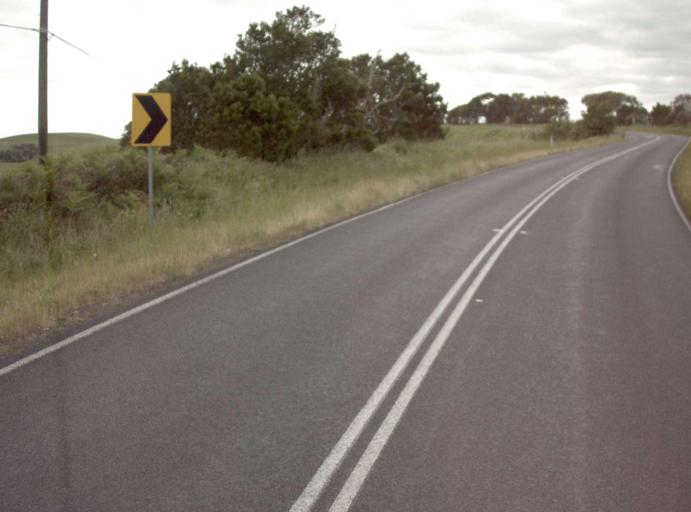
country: AU
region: Victoria
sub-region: Bass Coast
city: North Wonthaggi
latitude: -38.4607
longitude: 145.7881
